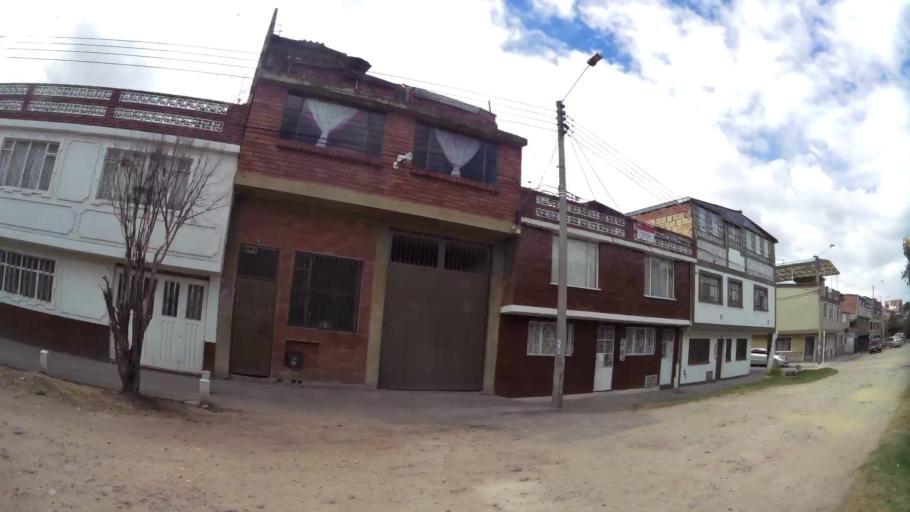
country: CO
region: Bogota D.C.
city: Bogota
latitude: 4.6005
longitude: -74.1260
